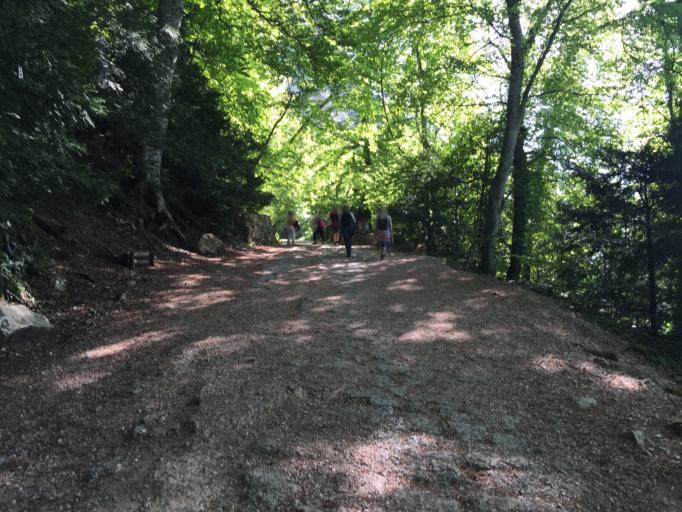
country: FR
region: Provence-Alpes-Cote d'Azur
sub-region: Departement du Var
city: Nans-les-Pins
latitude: 43.3279
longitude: 5.7647
